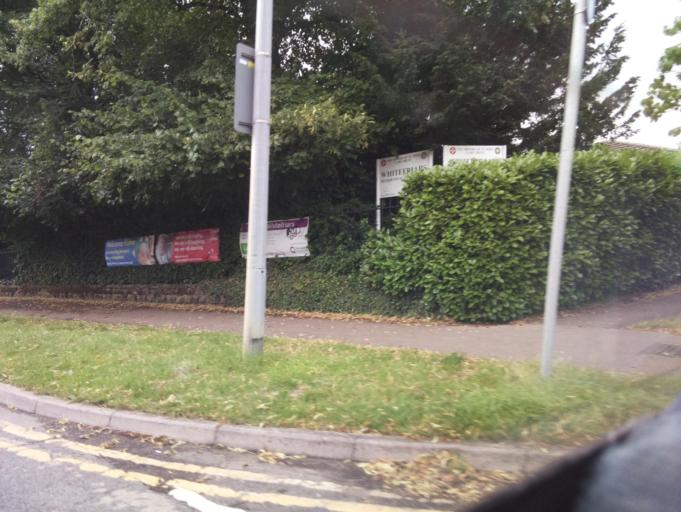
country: GB
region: England
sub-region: Lincolnshire
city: Stamford
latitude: 52.6573
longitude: -0.4674
